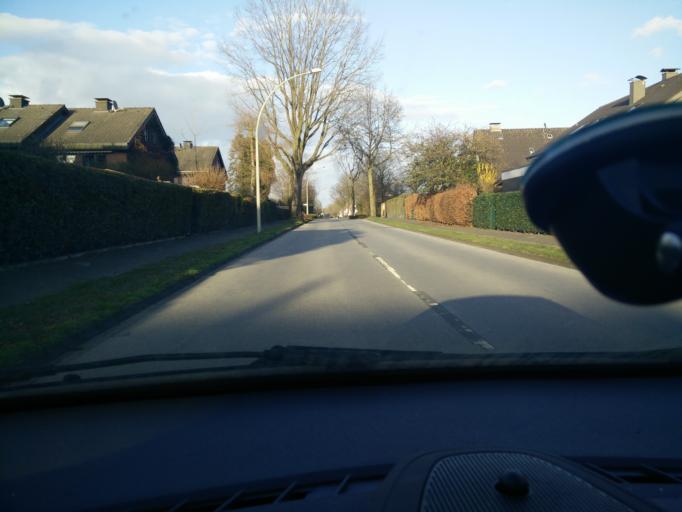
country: DE
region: North Rhine-Westphalia
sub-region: Regierungsbezirk Munster
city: Raesfeld
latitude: 51.7706
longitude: 6.8341
